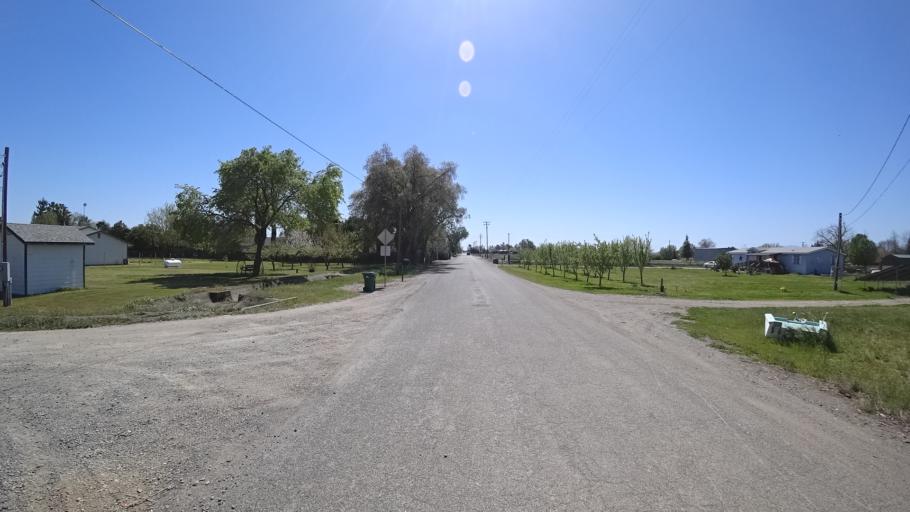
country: US
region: California
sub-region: Glenn County
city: Orland
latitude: 39.7657
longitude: -122.2297
